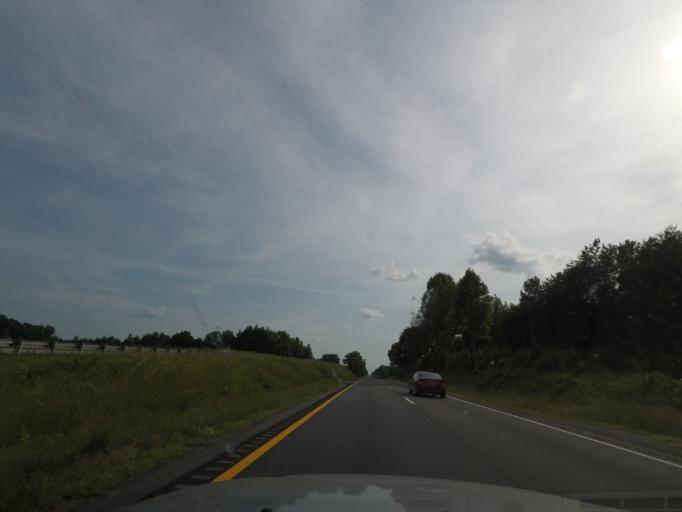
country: US
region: Virginia
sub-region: Mecklenburg County
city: Chase City
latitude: 36.9189
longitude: -78.5191
